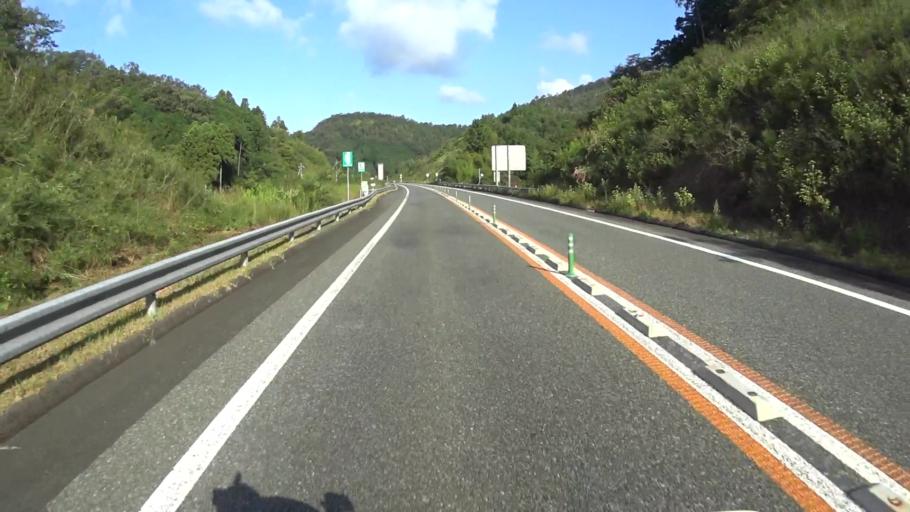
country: JP
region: Kyoto
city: Ayabe
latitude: 35.3407
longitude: 135.3046
